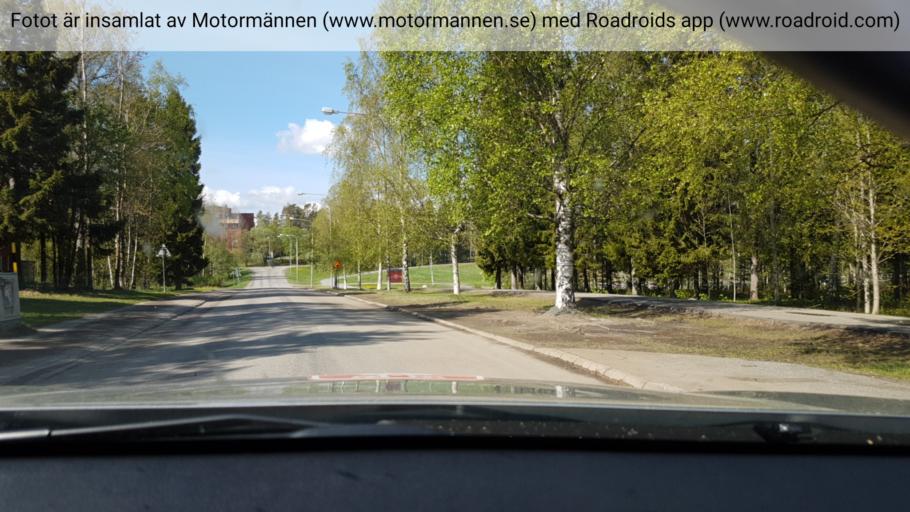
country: SE
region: Vaesterbotten
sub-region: Umea Kommun
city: Ersmark
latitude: 63.8593
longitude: 20.3198
